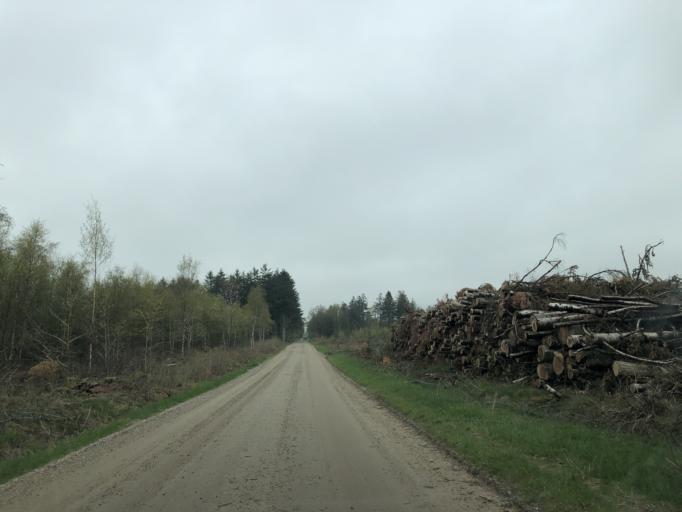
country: DK
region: Central Jutland
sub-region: Lemvig Kommune
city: Lemvig
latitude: 56.5042
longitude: 8.3270
